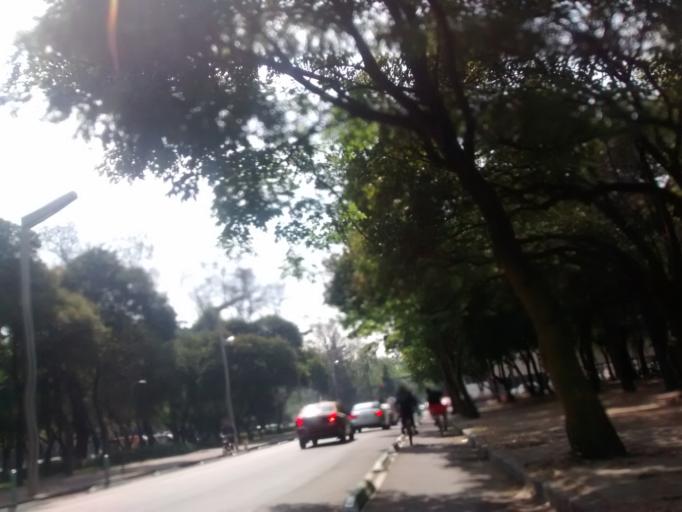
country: MX
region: Mexico City
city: Polanco
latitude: 19.4250
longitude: -99.1803
